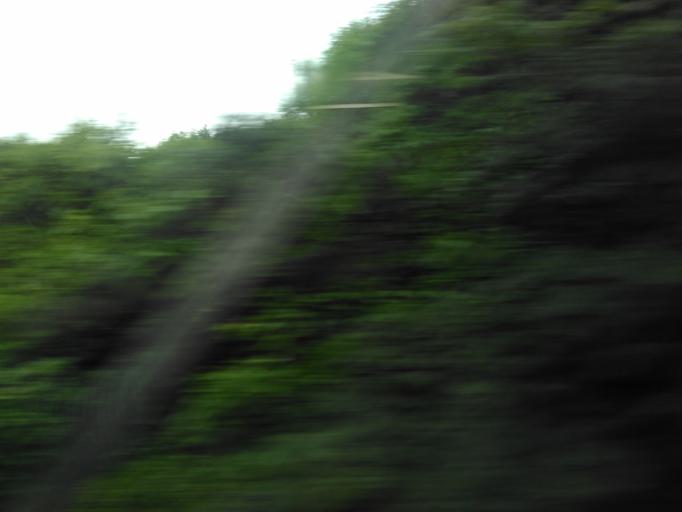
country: GB
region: Scotland
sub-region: East Lothian
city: Musselburgh
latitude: 55.9388
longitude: -3.0844
